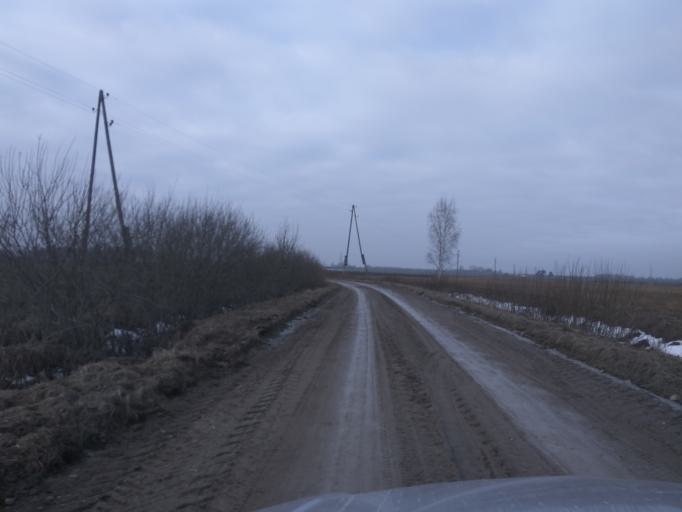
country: LV
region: Durbe
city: Liegi
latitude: 56.6692
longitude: 21.3743
